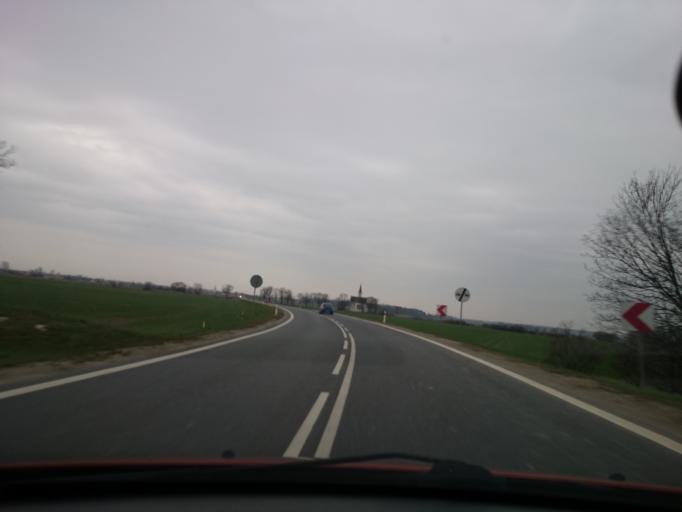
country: PL
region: Opole Voivodeship
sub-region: Powiat nyski
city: Sidzina
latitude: 50.5845
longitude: 17.4691
